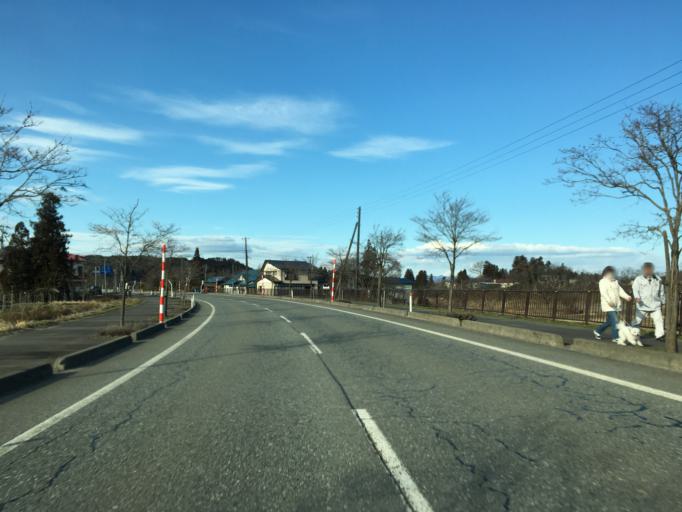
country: JP
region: Yamagata
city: Nagai
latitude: 38.0102
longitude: 139.9645
